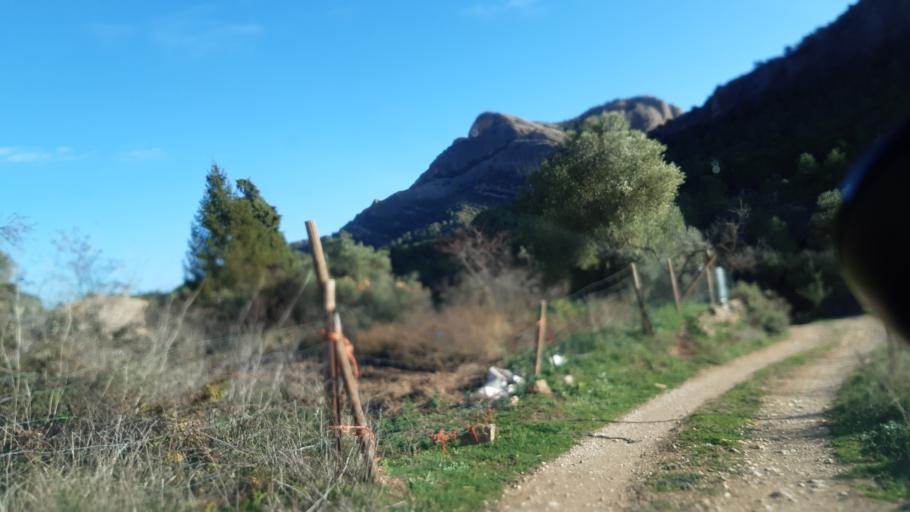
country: ES
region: Aragon
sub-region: Provincia de Teruel
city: Lledo
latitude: 40.8635
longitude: 0.2518
